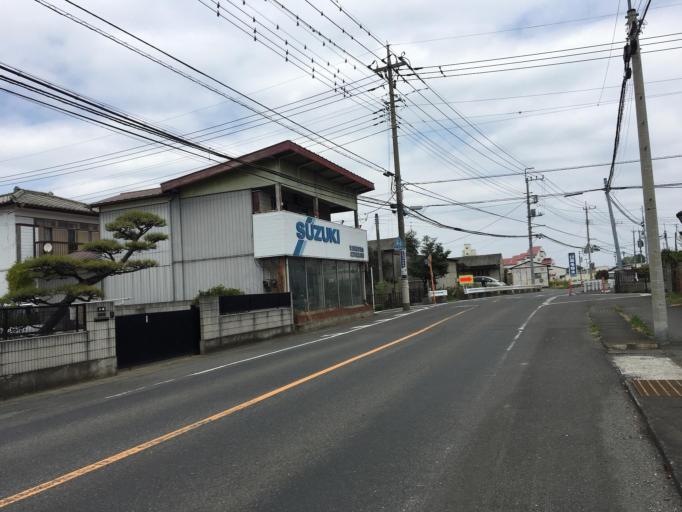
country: JP
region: Gunma
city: Isesaki
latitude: 36.2920
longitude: 139.1730
